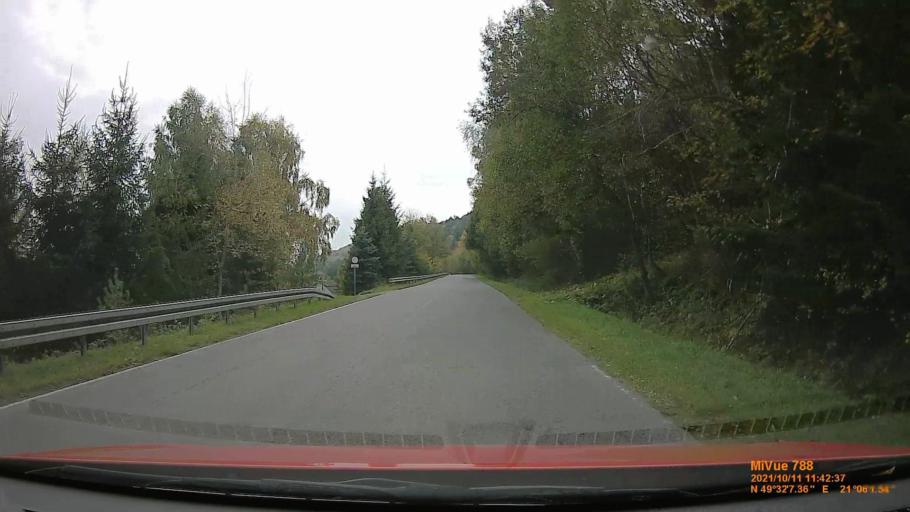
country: PL
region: Lesser Poland Voivodeship
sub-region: Powiat gorlicki
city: Uscie Gorlickie
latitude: 49.5352
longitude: 21.1006
